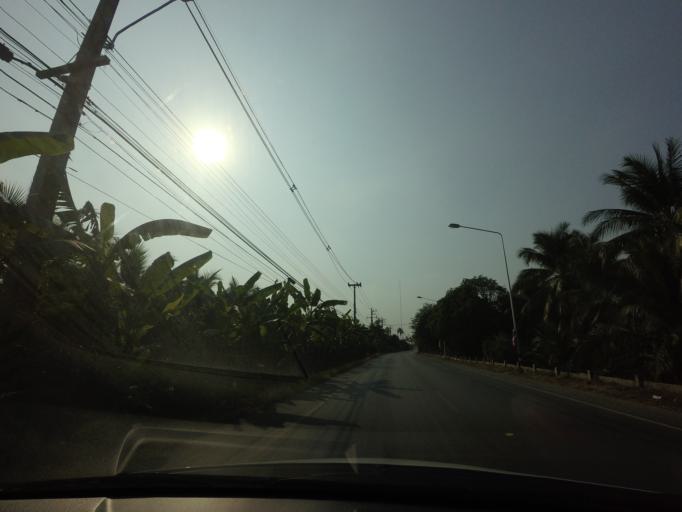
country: TH
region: Nakhon Pathom
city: Sam Phran
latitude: 13.6932
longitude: 100.2177
